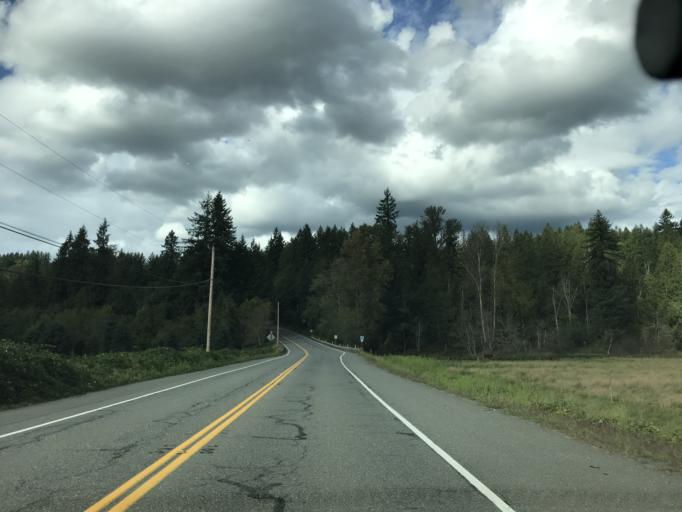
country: US
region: Washington
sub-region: King County
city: Black Diamond
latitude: 47.2844
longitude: -122.0526
